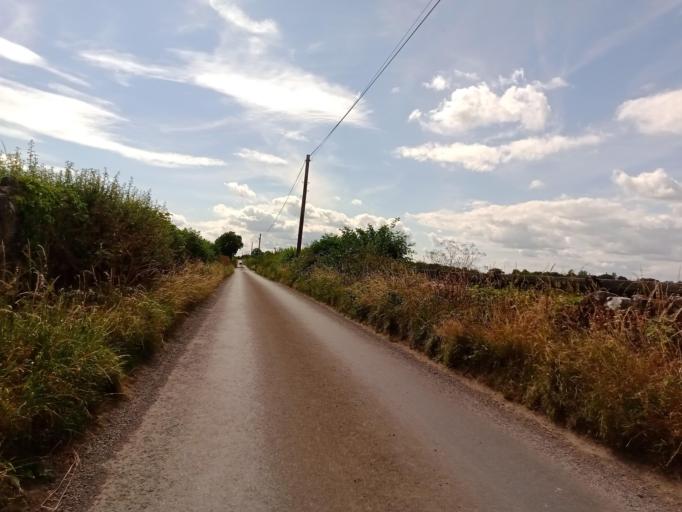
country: IE
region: Leinster
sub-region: Kilkenny
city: Kilkenny
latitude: 52.6364
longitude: -7.2164
